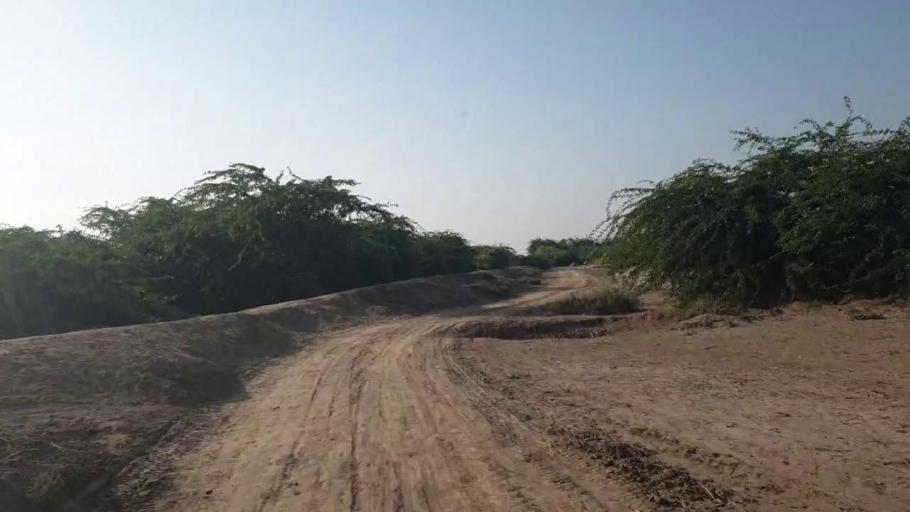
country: PK
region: Sindh
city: Badin
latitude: 24.4602
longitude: 68.7360
